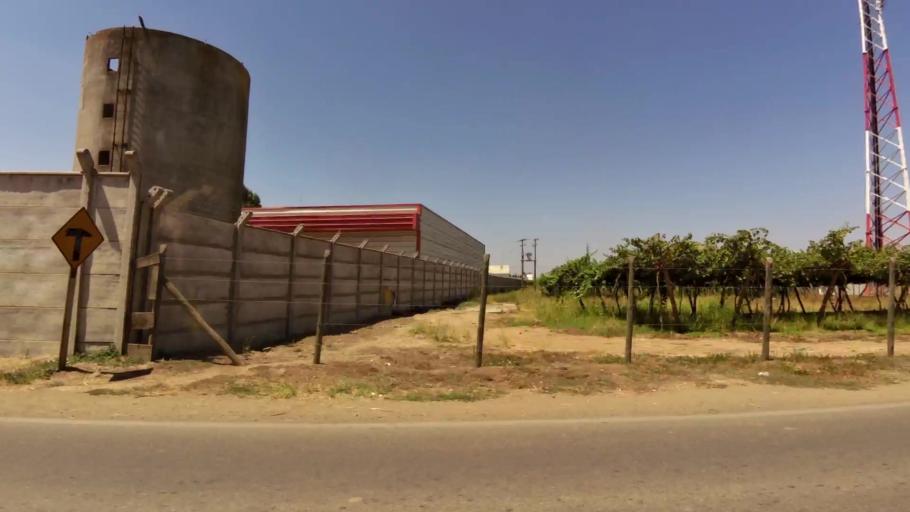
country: CL
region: Maule
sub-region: Provincia de Talca
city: Talca
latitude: -35.4411
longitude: -71.6139
